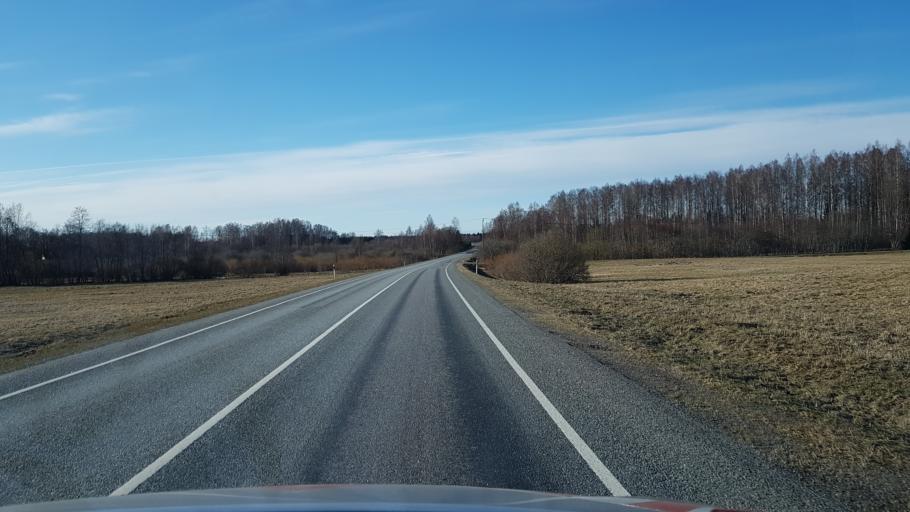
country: EE
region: Laeaene-Virumaa
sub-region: Tapa vald
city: Tapa
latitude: 59.4451
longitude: 25.9514
